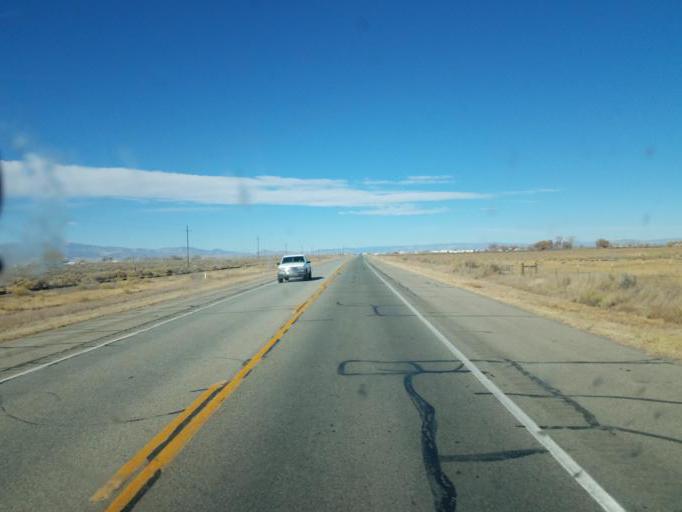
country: US
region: Colorado
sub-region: Alamosa County
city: Alamosa
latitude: 37.5101
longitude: -105.9770
